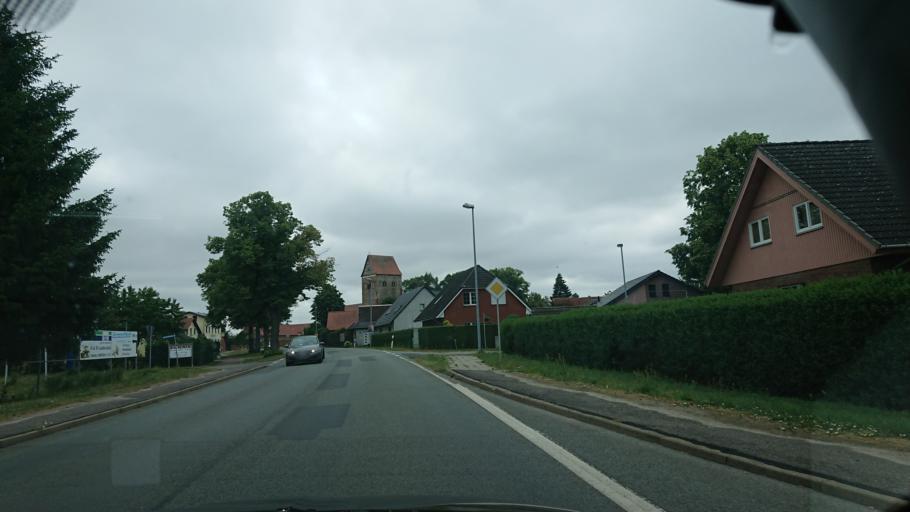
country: DE
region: Brandenburg
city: Perleberg
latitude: 53.0627
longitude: 11.8954
